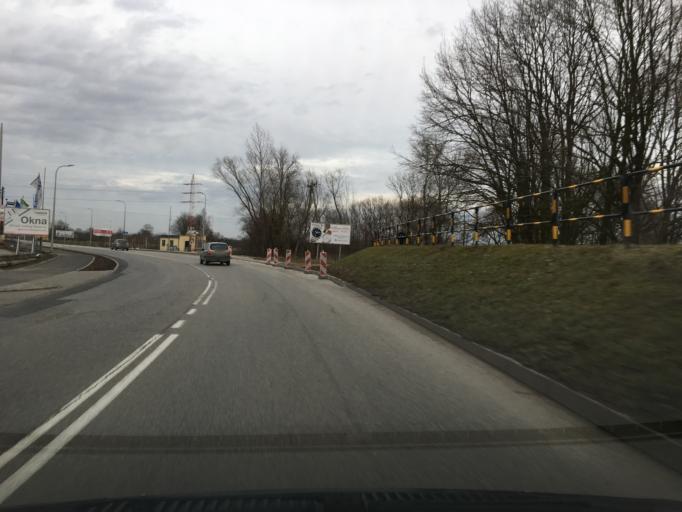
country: PL
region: Opole Voivodeship
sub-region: Powiat kedzierzynsko-kozielski
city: Kozle
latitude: 50.3380
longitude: 18.1590
